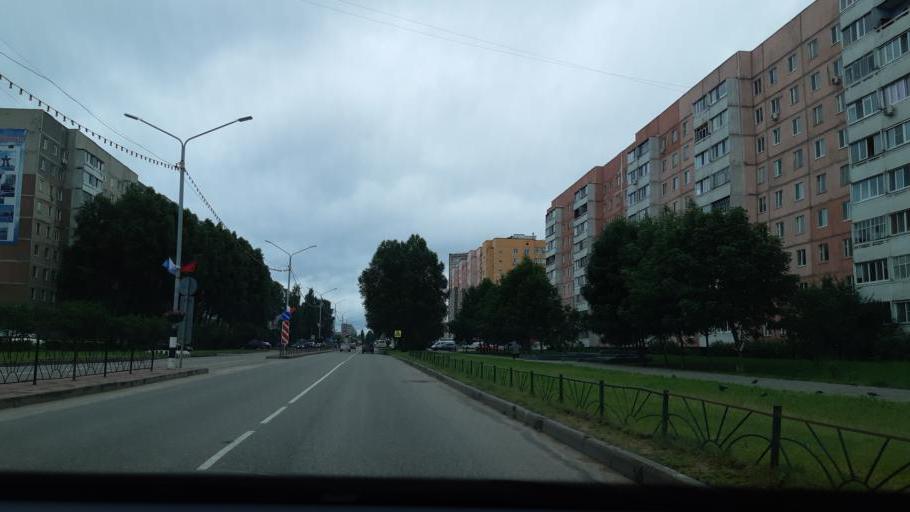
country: RU
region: Smolensk
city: Desnogorsk
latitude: 54.1474
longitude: 33.2836
